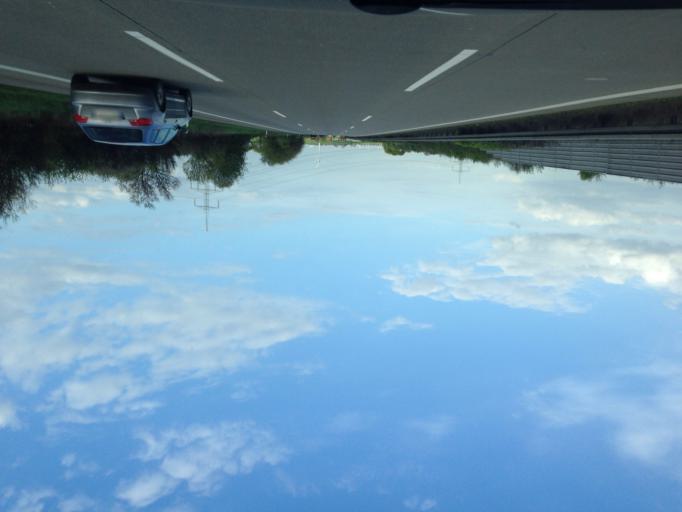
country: DE
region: Saxony-Anhalt
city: Wefensleben
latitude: 52.2056
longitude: 11.1753
